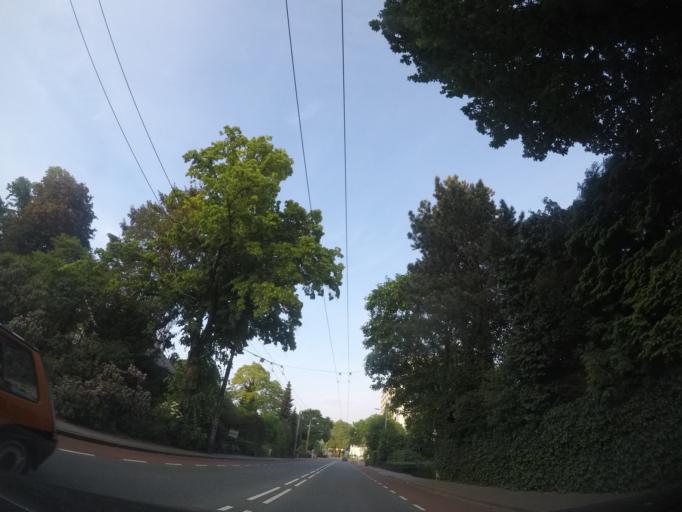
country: NL
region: Gelderland
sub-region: Gemeente Arnhem
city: Sterrenberg
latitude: 51.9834
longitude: 5.8776
